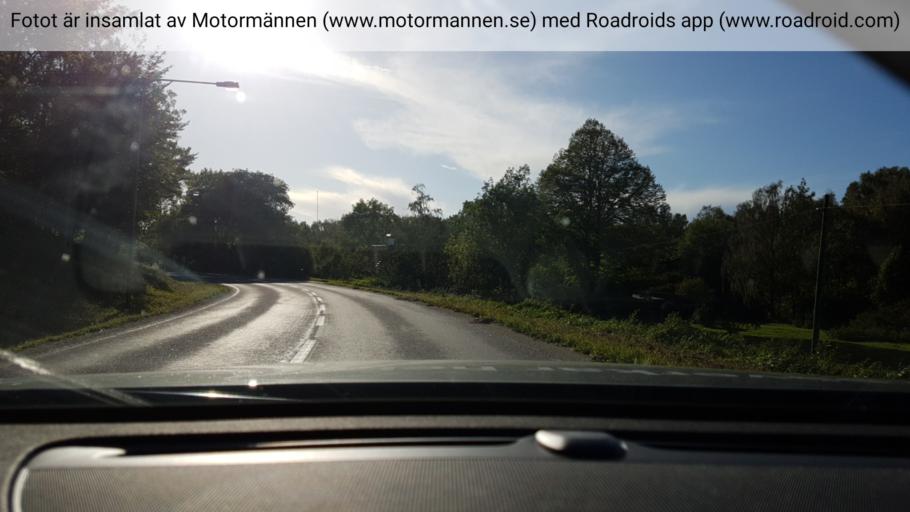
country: SE
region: Gotland
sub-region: Gotland
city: Klintehamn
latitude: 57.3819
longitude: 18.2367
